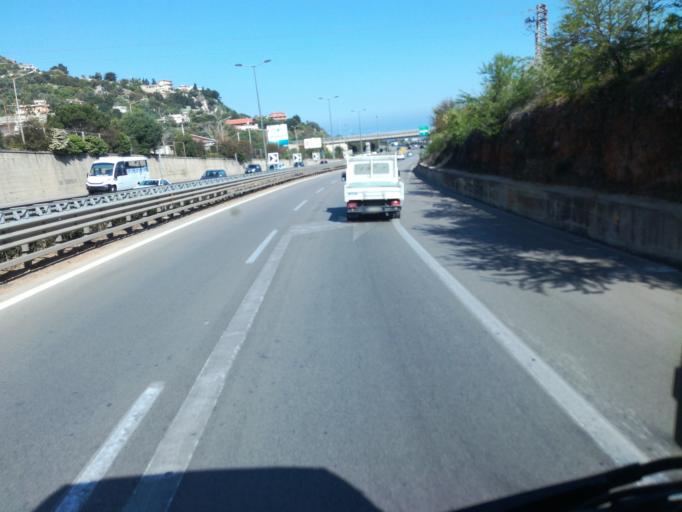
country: IT
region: Sicily
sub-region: Palermo
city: Isola delle Femmine
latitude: 38.1884
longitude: 13.2838
